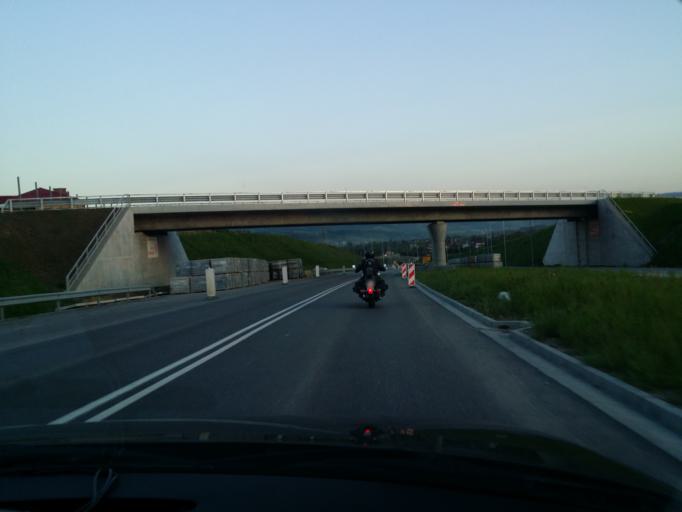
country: PL
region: Lesser Poland Voivodeship
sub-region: Powiat nowotarski
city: Rokiciny
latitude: 49.6087
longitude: 19.9258
